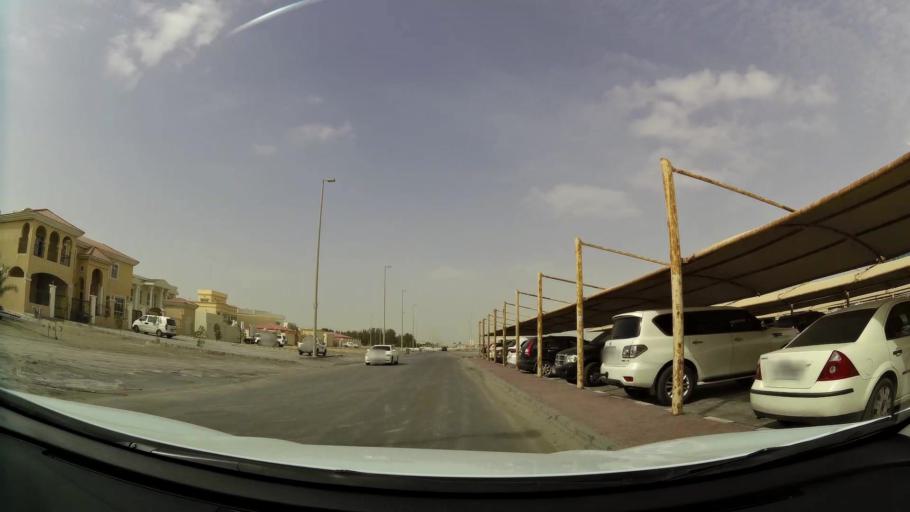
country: AE
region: Abu Dhabi
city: Abu Dhabi
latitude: 24.4063
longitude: 54.5684
